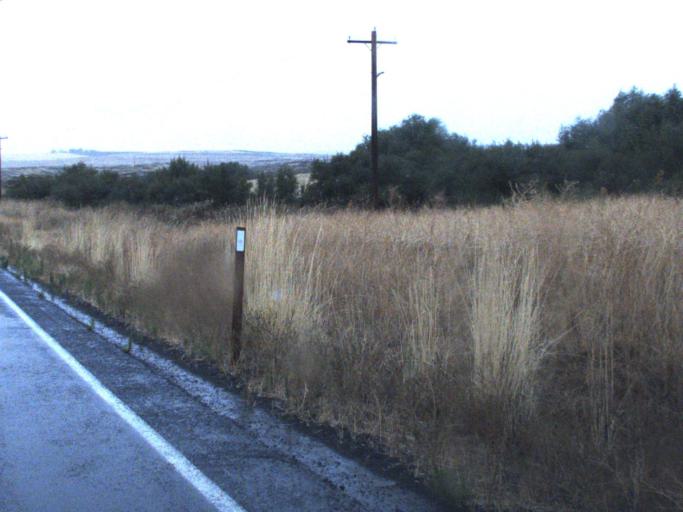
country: US
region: Washington
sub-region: Lincoln County
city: Davenport
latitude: 47.3500
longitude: -118.0962
